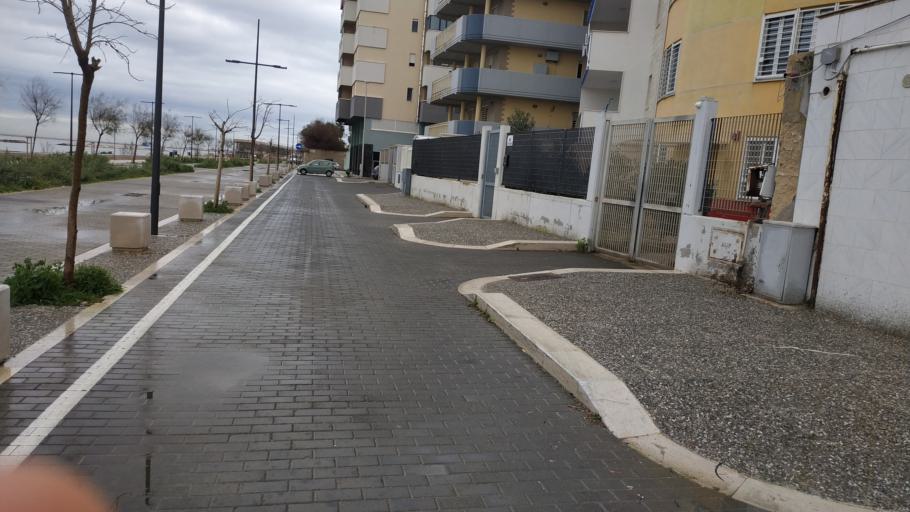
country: IT
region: Apulia
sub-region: Provincia di Bari
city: San Paolo
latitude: 41.1396
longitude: 16.8138
